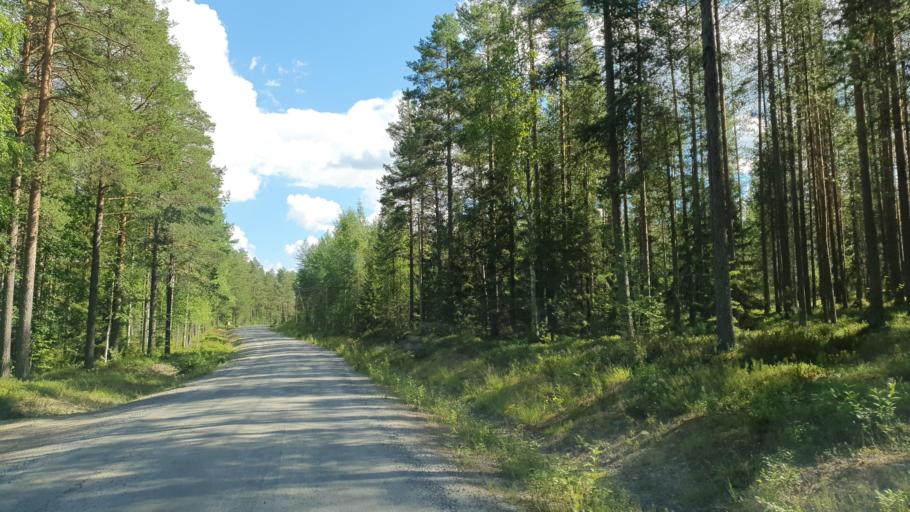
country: FI
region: Kainuu
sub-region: Kehys-Kainuu
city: Kuhmo
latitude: 64.1060
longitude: 29.3955
